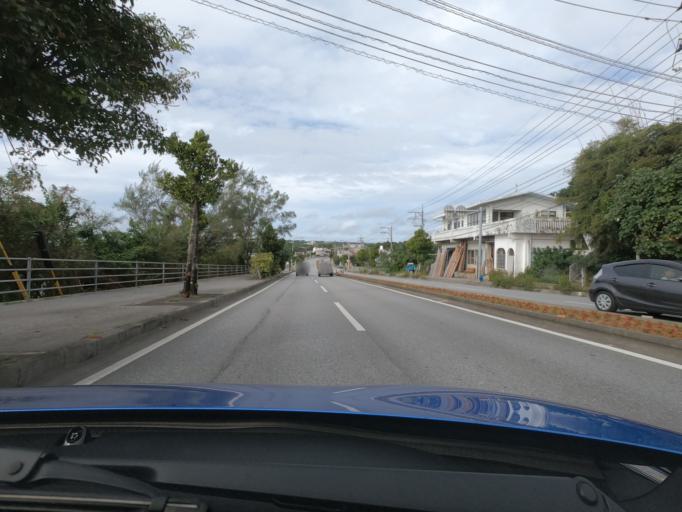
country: JP
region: Okinawa
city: Nago
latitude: 26.6683
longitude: 127.8900
